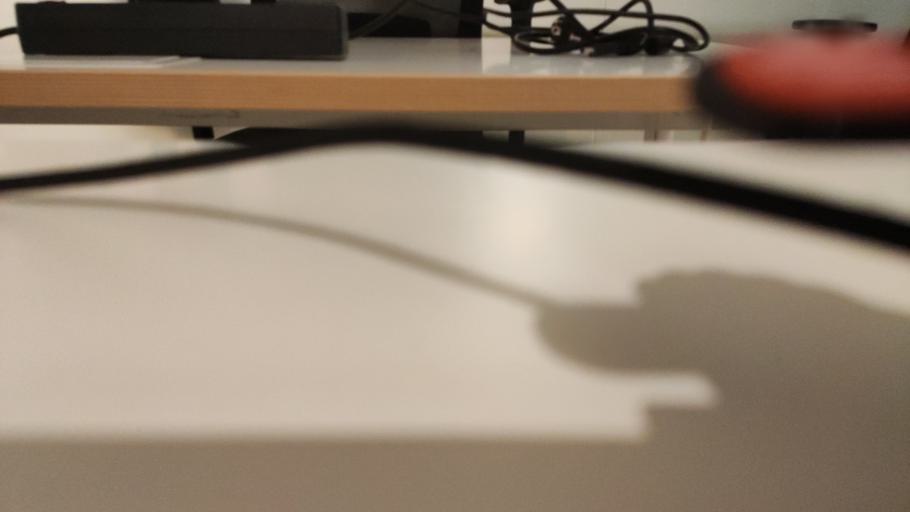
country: RU
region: Moskovskaya
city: Proletarskiy
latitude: 54.9854
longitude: 37.3224
